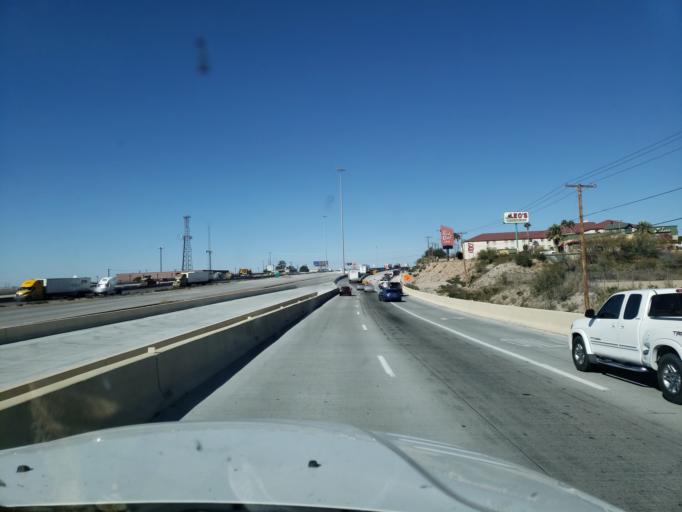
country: US
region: New Mexico
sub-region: Dona Ana County
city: Sunland Park
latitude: 31.8338
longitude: -106.5672
